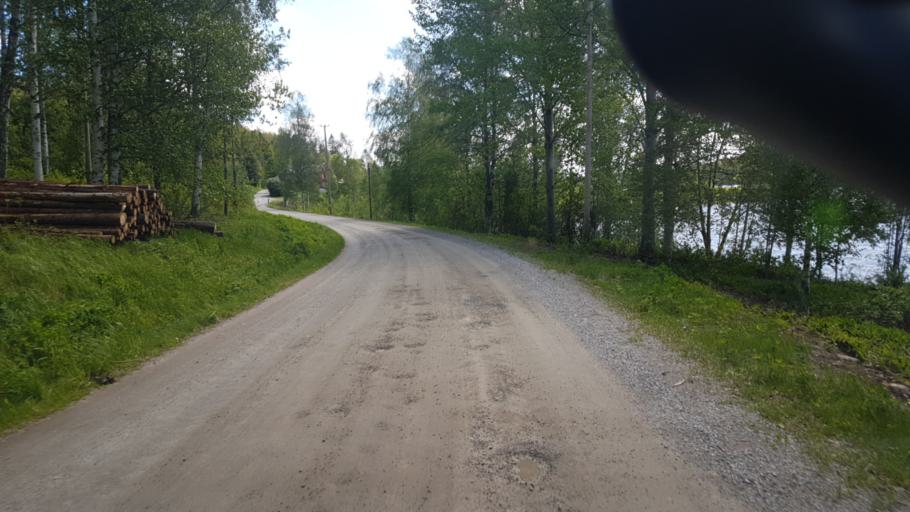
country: SE
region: Vaermland
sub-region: Arvika Kommun
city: Arvika
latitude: 59.7363
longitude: 12.8303
